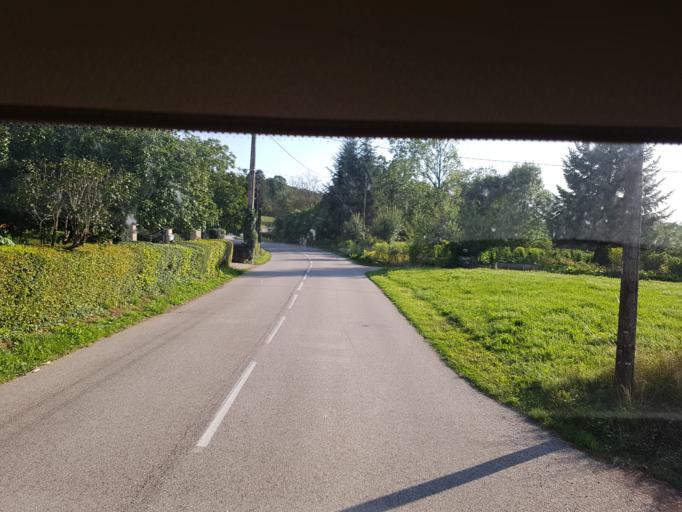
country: FR
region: Rhone-Alpes
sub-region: Departement de l'Ain
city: Neuville-sur-Ain
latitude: 46.0981
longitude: 5.3831
